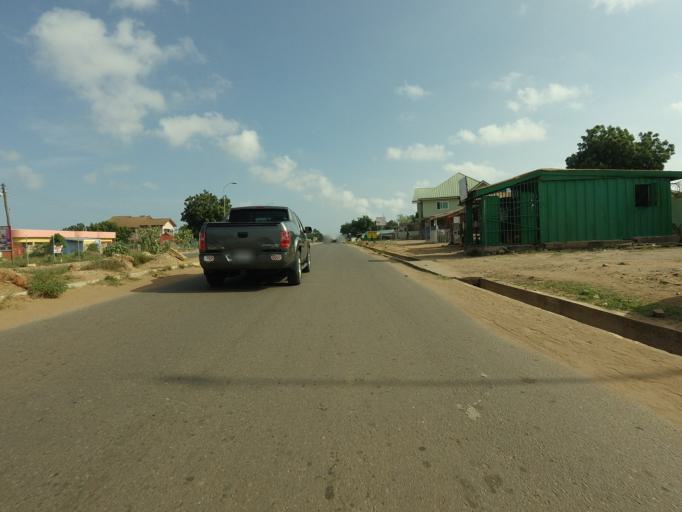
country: GH
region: Greater Accra
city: Tema
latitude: 5.6633
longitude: -0.0502
